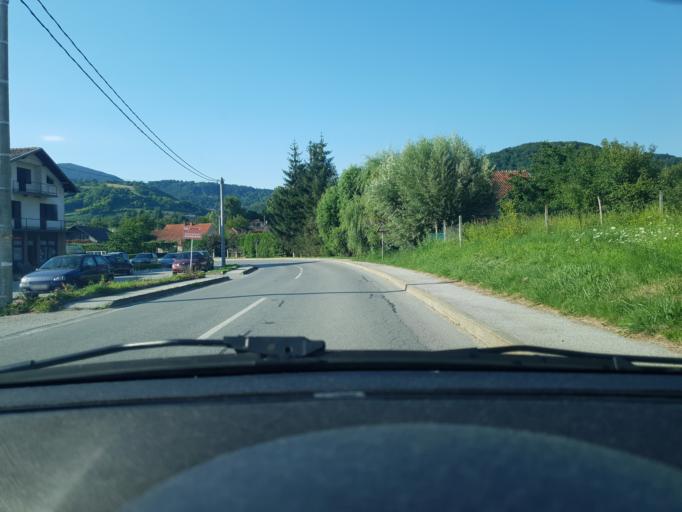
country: HR
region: Krapinsko-Zagorska
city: Radoboj
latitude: 46.1544
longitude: 15.9425
